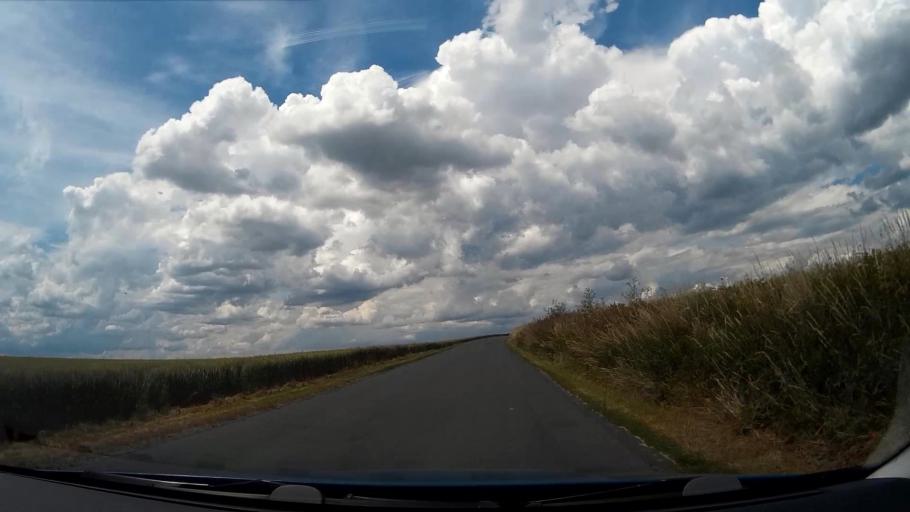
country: CZ
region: South Moravian
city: Orechov
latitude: 49.0864
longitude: 16.5347
